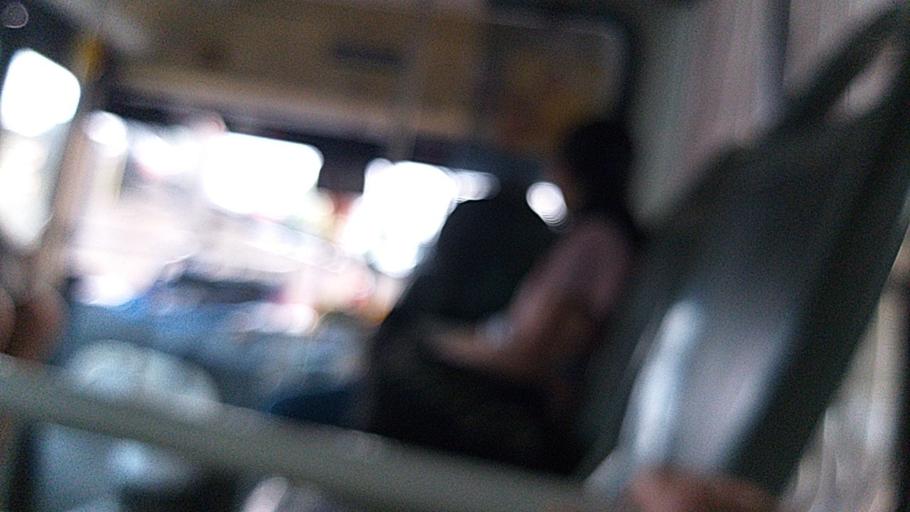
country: TH
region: Bangkok
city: Don Mueang
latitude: 13.9239
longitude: 100.6055
